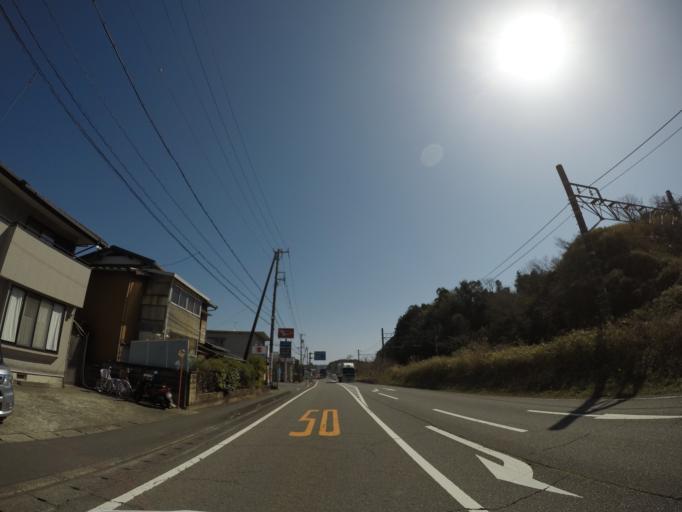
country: JP
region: Shizuoka
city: Kakegawa
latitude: 34.7621
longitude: 138.0694
